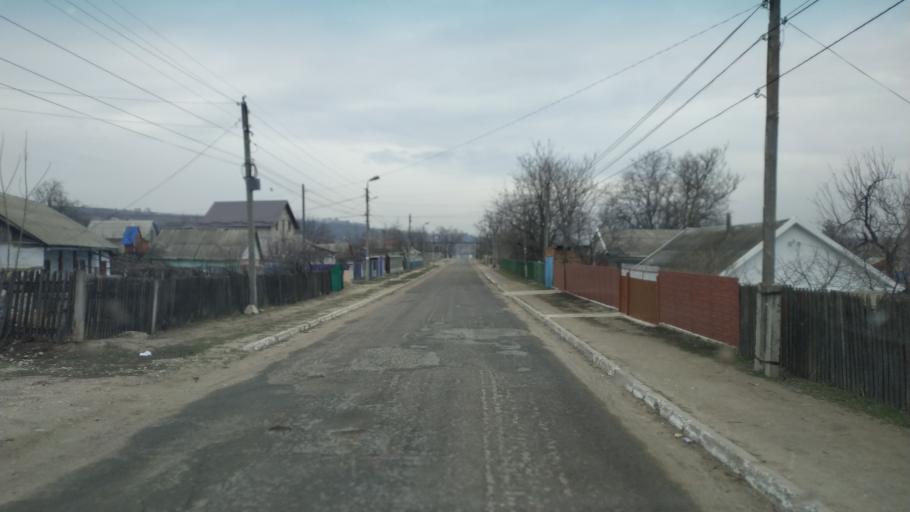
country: MD
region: Chisinau
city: Singera
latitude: 46.9335
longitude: 28.9964
